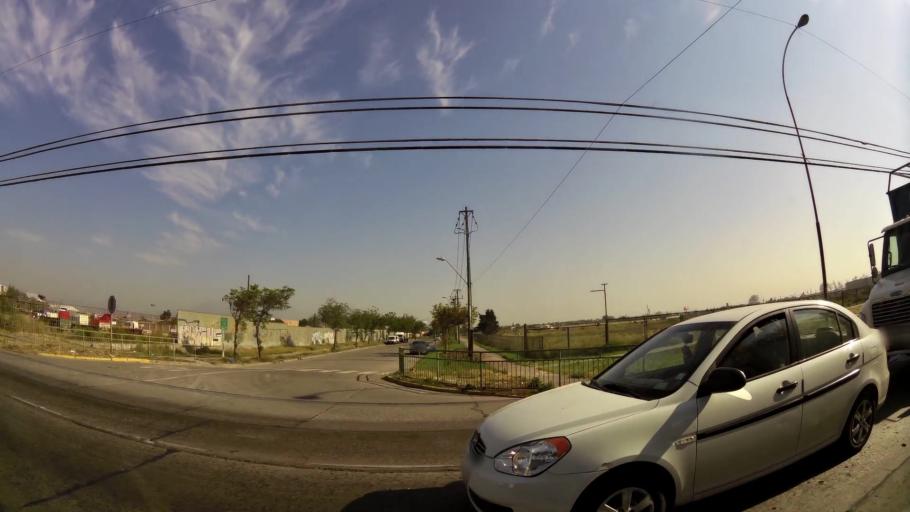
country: CL
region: Santiago Metropolitan
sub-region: Provincia de Santiago
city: Lo Prado
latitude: -33.5184
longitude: -70.7402
